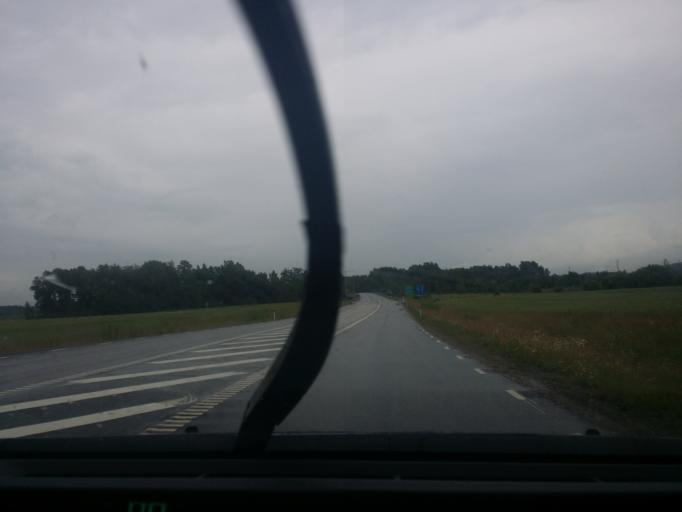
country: SE
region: Vaestmanland
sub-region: Arboga Kommun
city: Arboga
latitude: 59.4133
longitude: 15.7615
